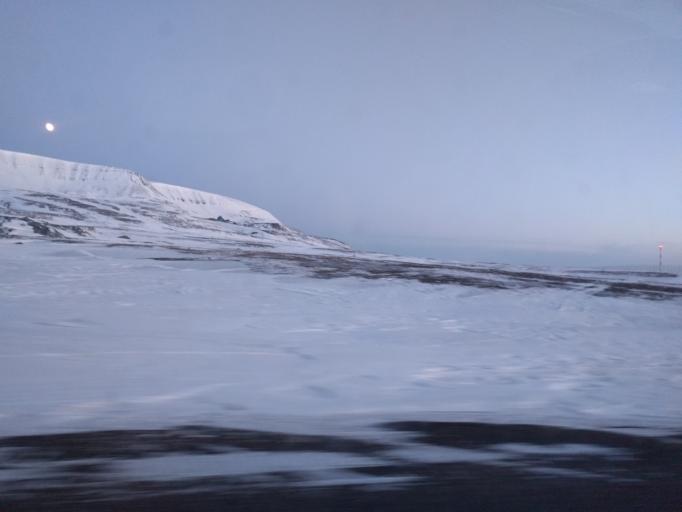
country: SJ
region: Svalbard
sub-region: Spitsbergen
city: Longyearbyen
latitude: 78.2412
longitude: 15.5179
